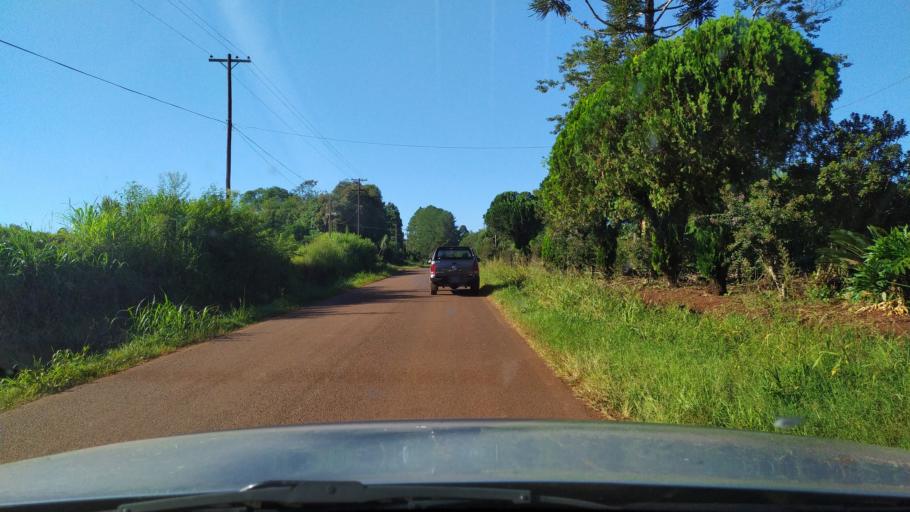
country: AR
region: Misiones
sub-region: Departamento de Montecarlo
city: Montecarlo
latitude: -26.6012
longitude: -54.7021
